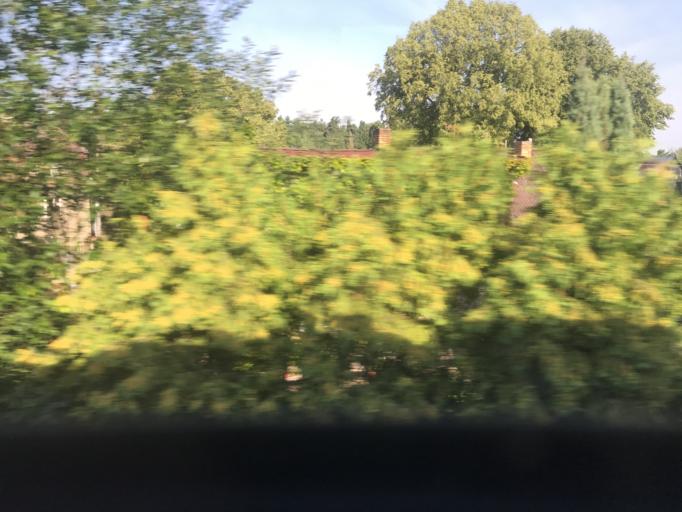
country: CZ
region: Jihocesky
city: Sobeslav
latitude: 49.3004
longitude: 14.7183
